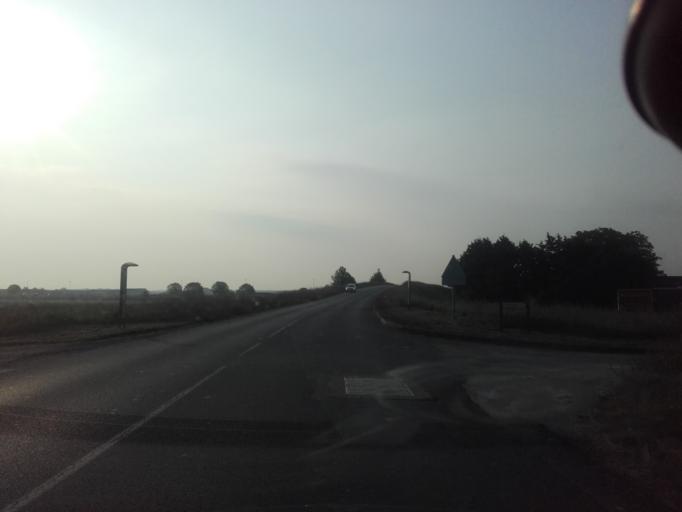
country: FR
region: Centre
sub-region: Departement d'Indre-et-Loire
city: Parcay-Meslay
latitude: 47.4476
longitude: 0.7371
